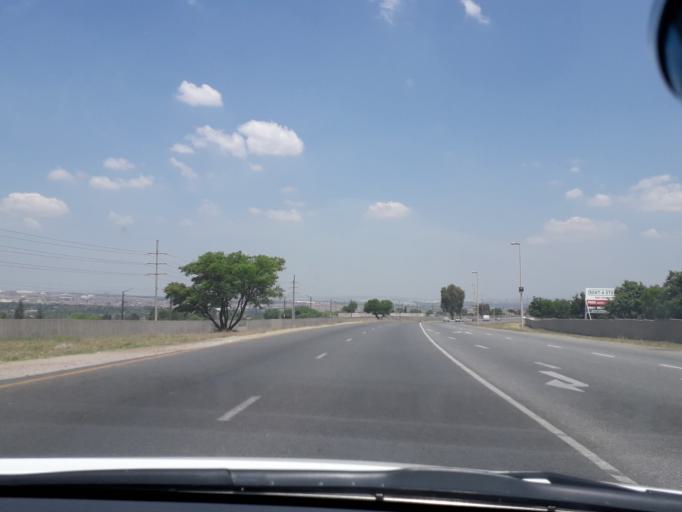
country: ZA
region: Gauteng
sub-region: City of Johannesburg Metropolitan Municipality
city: Midrand
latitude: -26.0012
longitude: 28.1371
